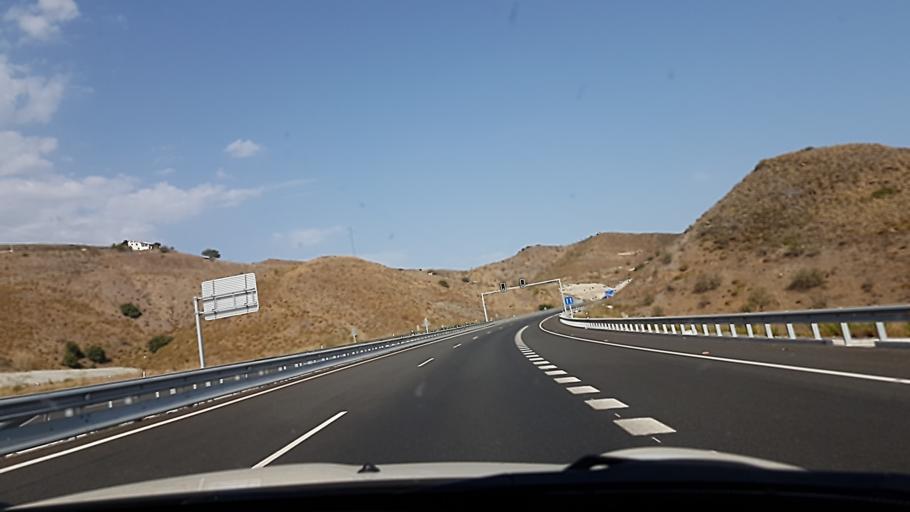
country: ES
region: Andalusia
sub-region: Provincia de Granada
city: Polopos
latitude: 36.7505
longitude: -3.3078
